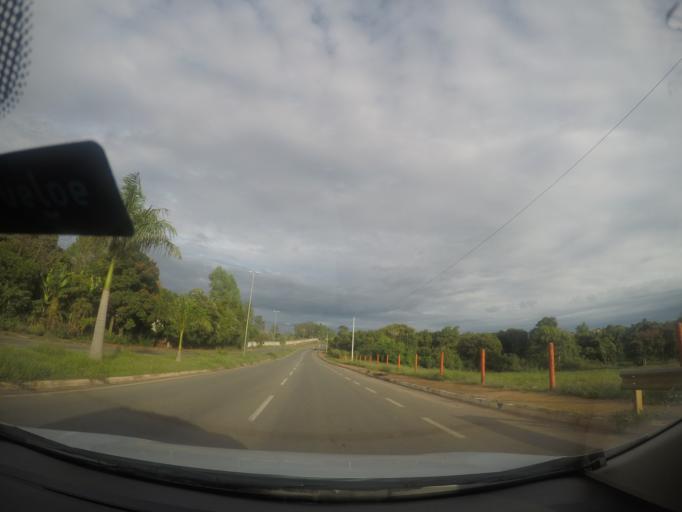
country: BR
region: Goias
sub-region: Goiania
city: Goiania
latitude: -16.6363
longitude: -49.3190
